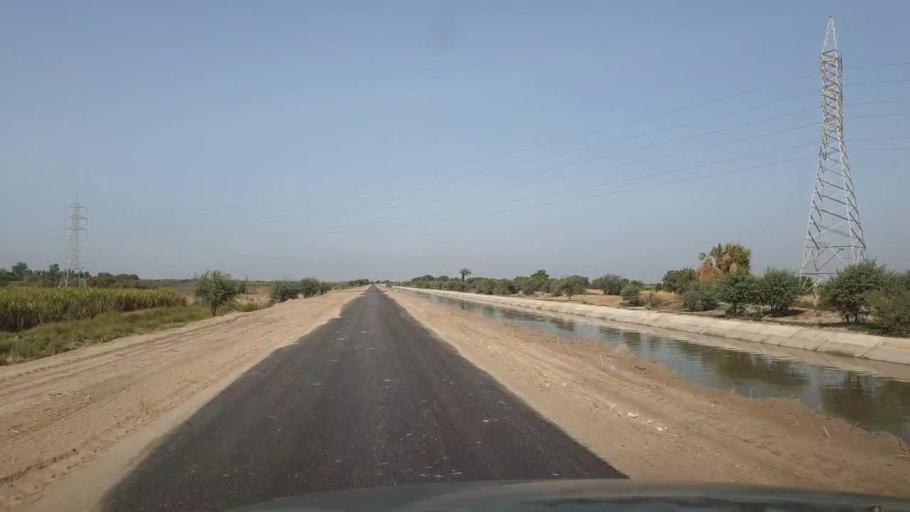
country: PK
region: Sindh
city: Tando Muhammad Khan
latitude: 25.1140
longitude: 68.3970
